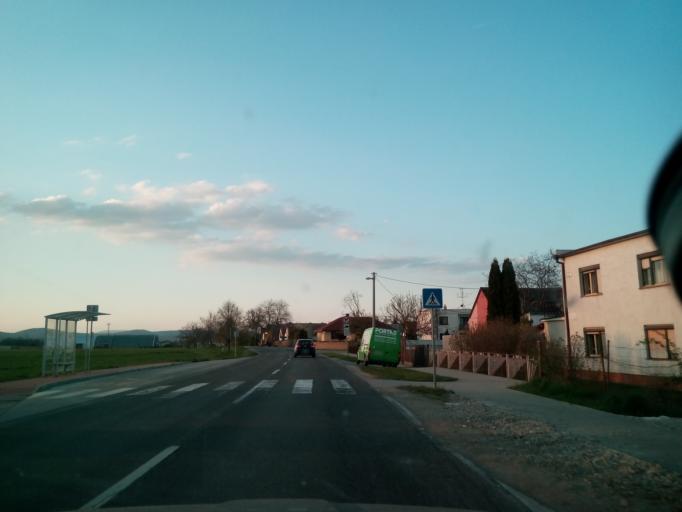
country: SK
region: Trnavsky
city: Vrbove
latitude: 48.5972
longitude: 17.7485
